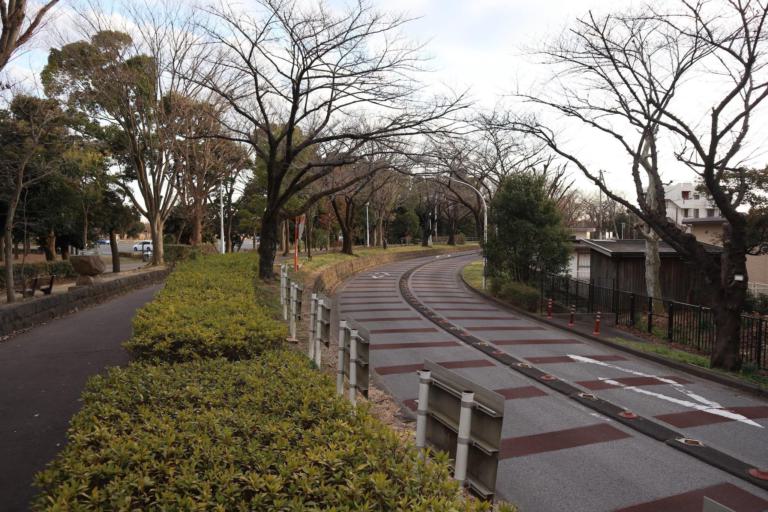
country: JP
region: Chiba
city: Matsudo
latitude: 35.7913
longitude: 139.8683
